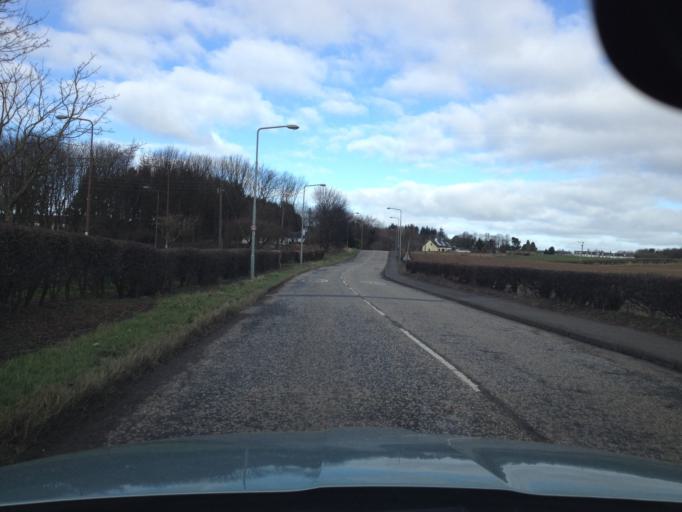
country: GB
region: Scotland
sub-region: West Lothian
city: Mid Calder
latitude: 55.8983
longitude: -3.4843
